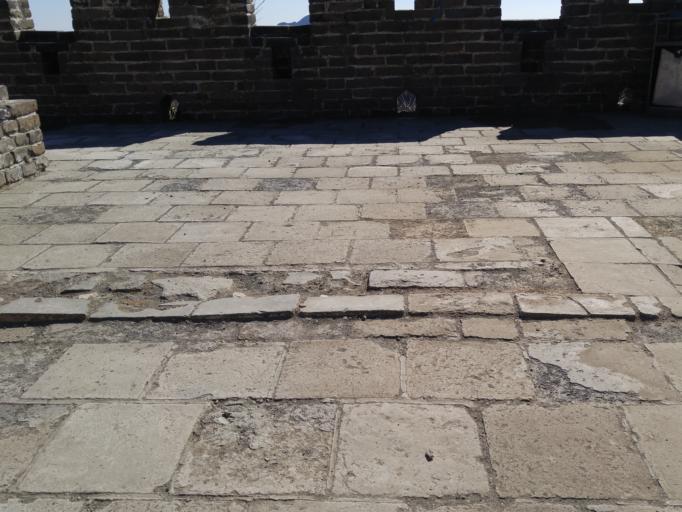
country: CN
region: Beijing
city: Bohai
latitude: 40.4475
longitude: 116.5547
